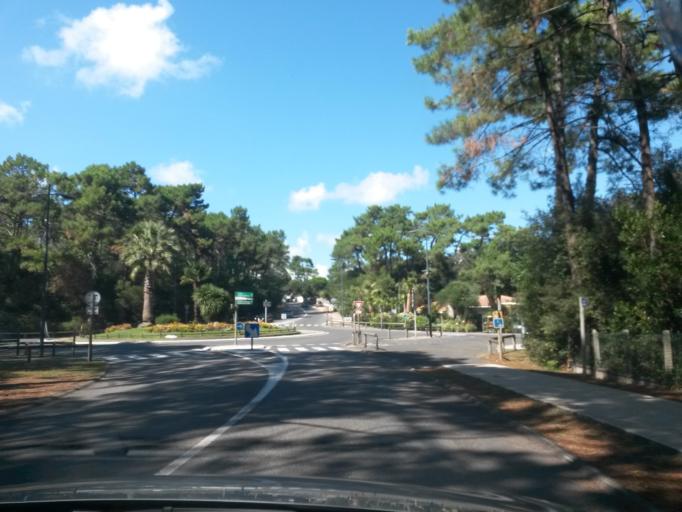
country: FR
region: Aquitaine
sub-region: Departement de la Gironde
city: Arcachon
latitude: 44.6859
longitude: -1.2375
